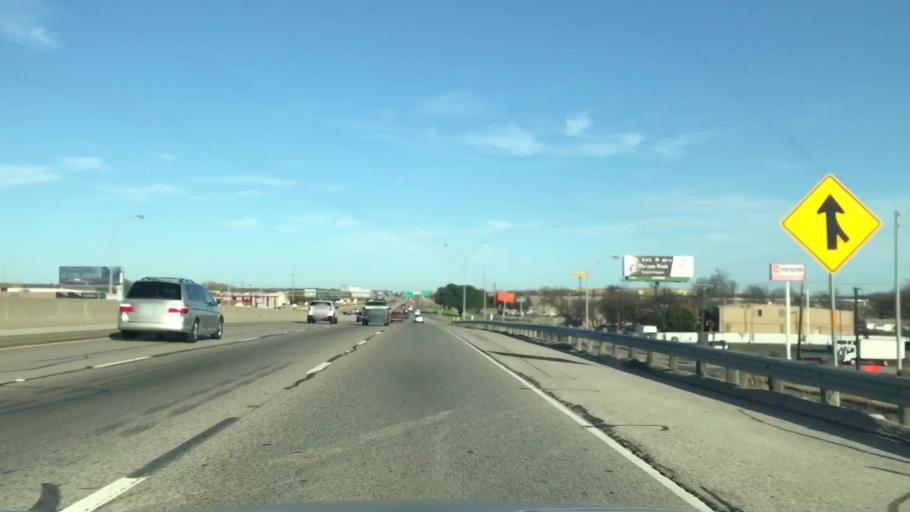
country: US
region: Texas
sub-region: Tarrant County
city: Haltom City
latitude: 32.7893
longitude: -97.2554
